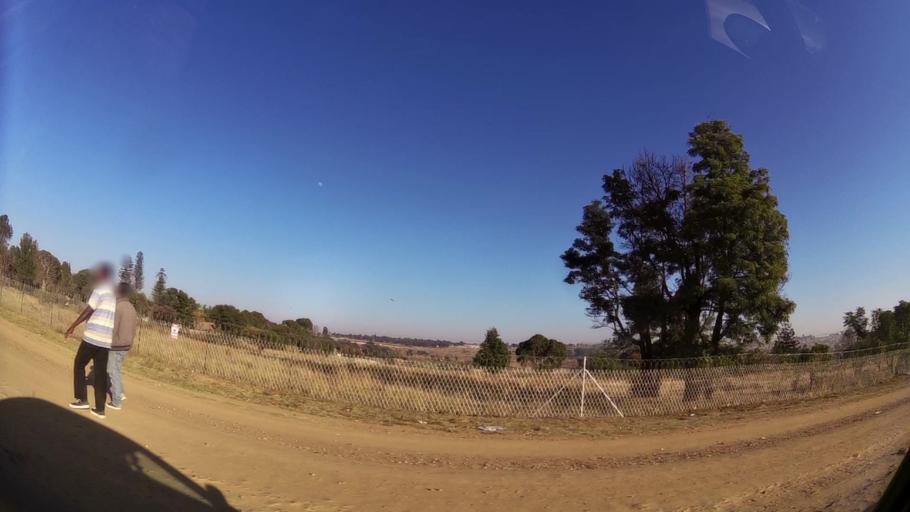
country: ZA
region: Gauteng
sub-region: City of Johannesburg Metropolitan Municipality
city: Midrand
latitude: -25.9312
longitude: 28.0971
